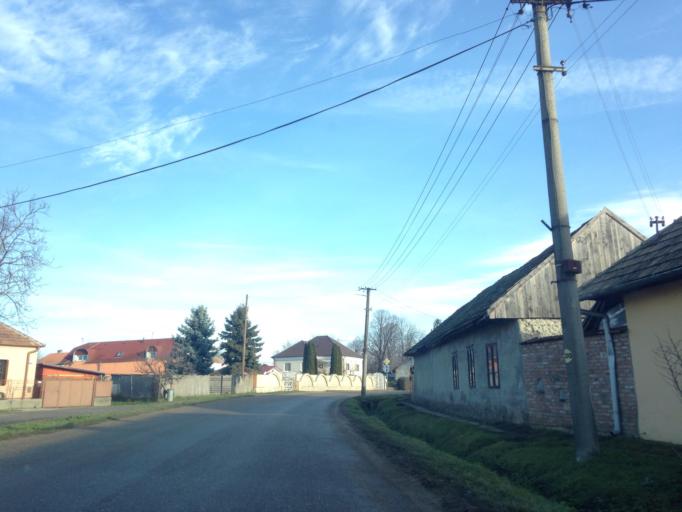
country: SK
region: Nitriansky
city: Svodin
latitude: 47.9307
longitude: 18.3987
